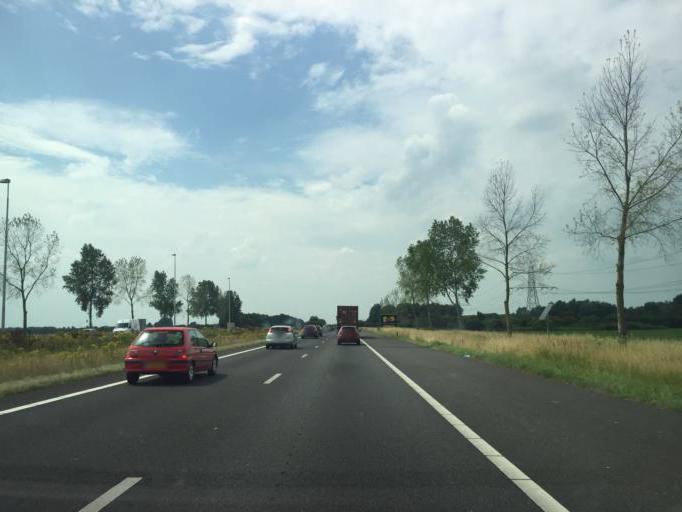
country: NL
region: Flevoland
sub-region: Gemeente Lelystad
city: Lelystad
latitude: 52.4676
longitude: 5.4768
